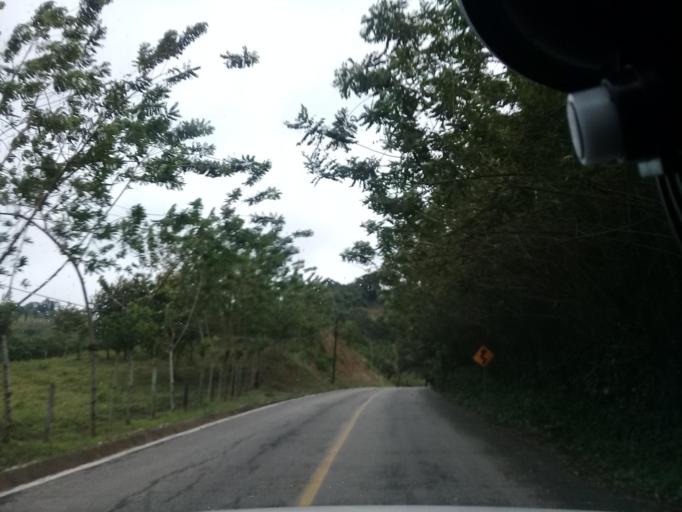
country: MX
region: Veracruz
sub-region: Chalma
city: San Pedro Coyutla
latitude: 21.2153
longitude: -98.4273
